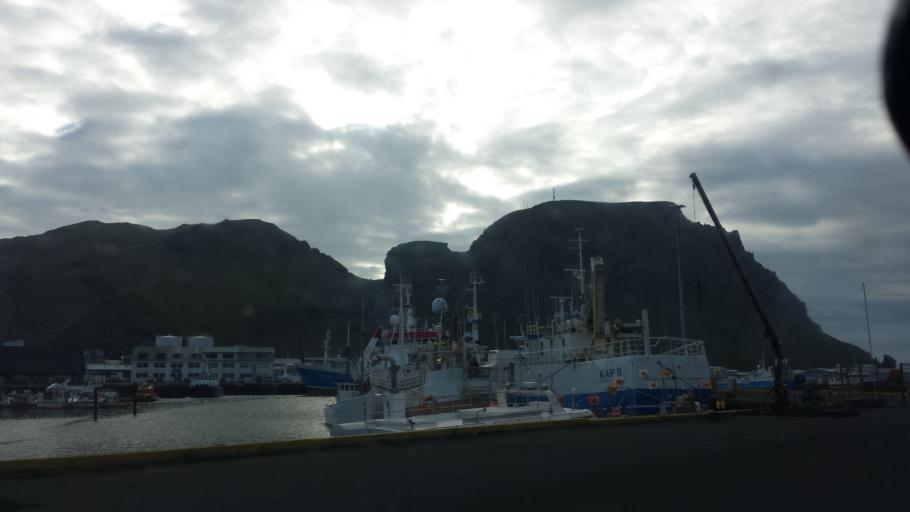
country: IS
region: South
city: Vestmannaeyjar
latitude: 63.4438
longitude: -20.2673
